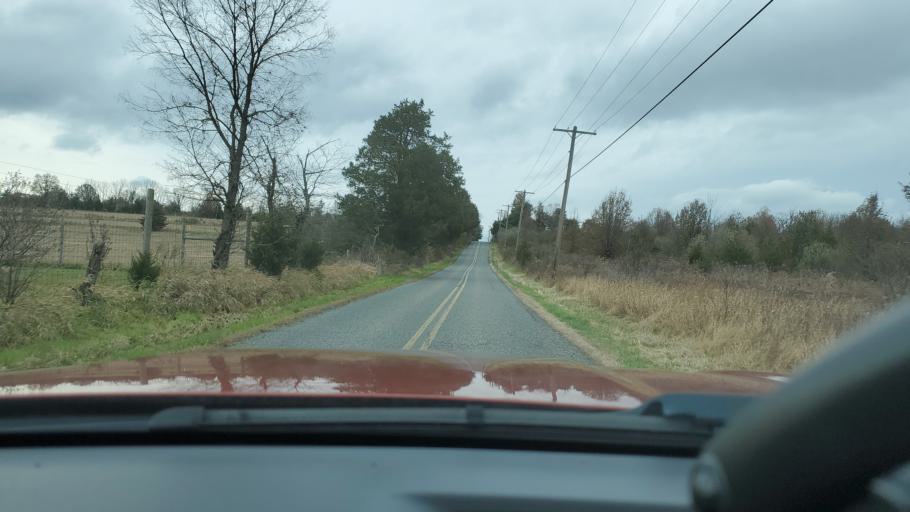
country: US
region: Pennsylvania
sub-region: Montgomery County
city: Spring Mount
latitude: 40.2958
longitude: -75.5034
